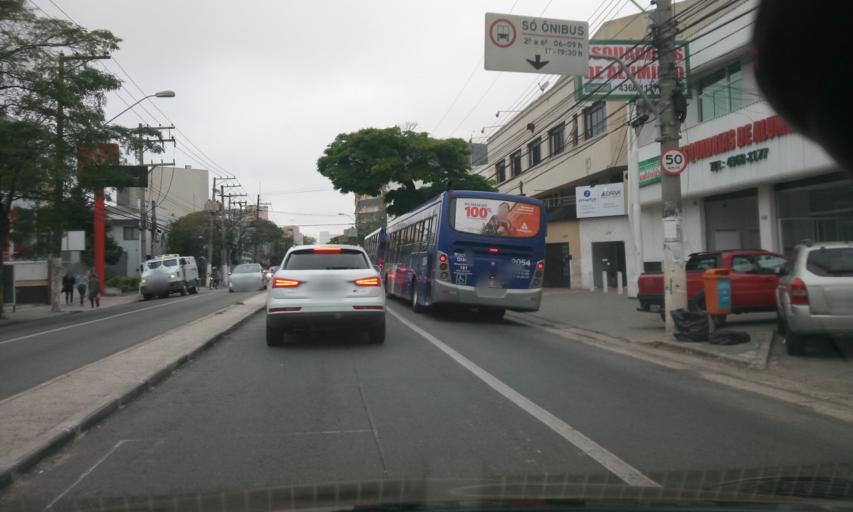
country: BR
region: Sao Paulo
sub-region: Sao Caetano Do Sul
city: Sao Caetano do Sul
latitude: -23.6519
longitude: -46.5749
